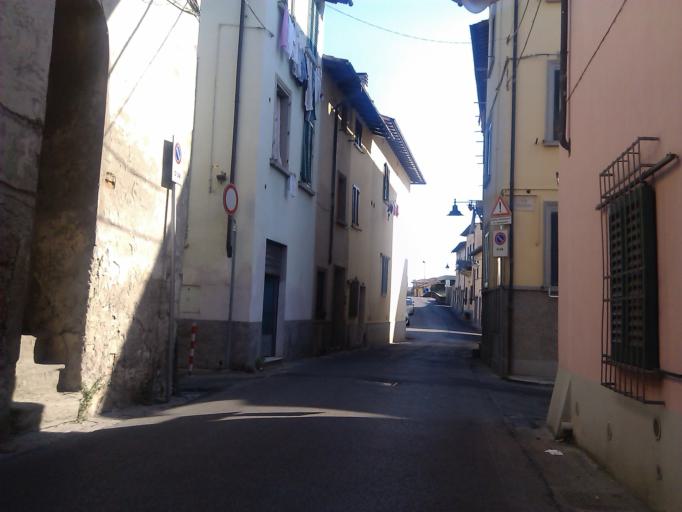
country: IT
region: Tuscany
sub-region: Province of Florence
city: Campi Bisenzio
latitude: 43.8398
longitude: 11.1330
